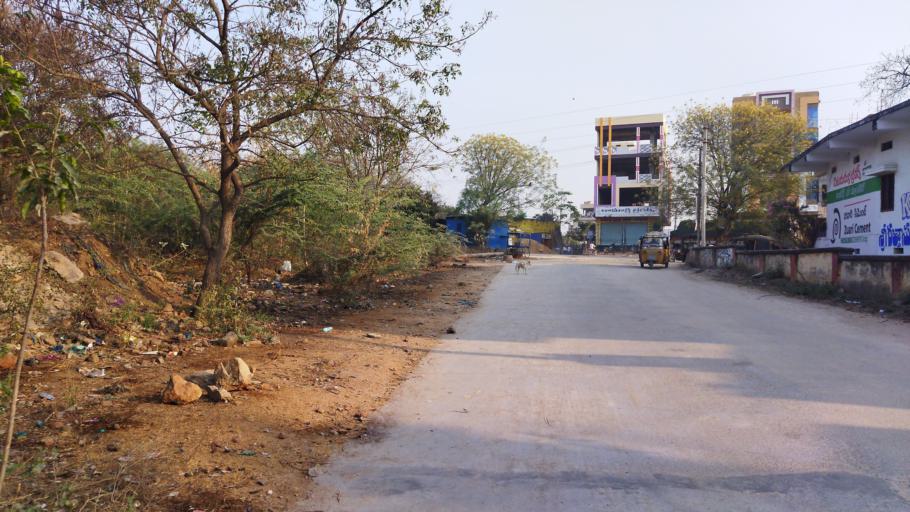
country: IN
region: Telangana
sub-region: Nalgonda
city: Nalgonda
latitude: 17.2334
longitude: 79.1243
